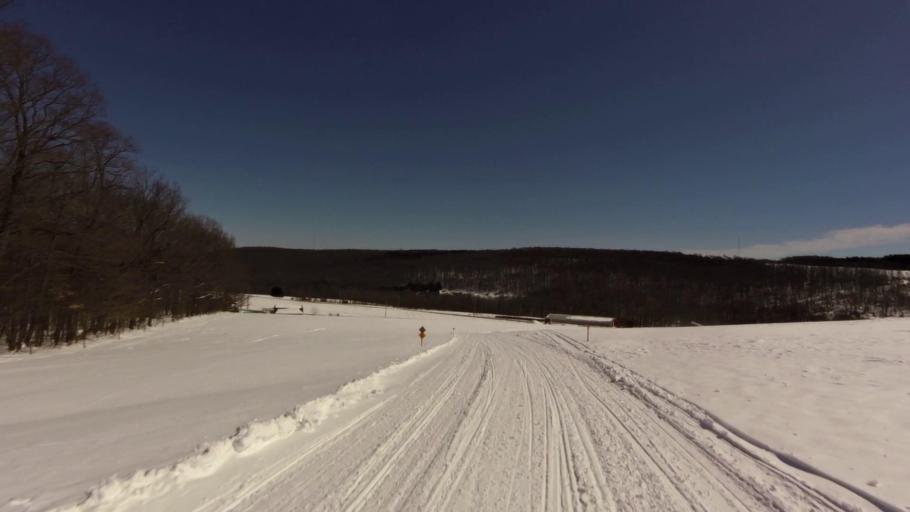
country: US
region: New York
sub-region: Allegany County
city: Houghton
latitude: 42.3672
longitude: -78.2542
